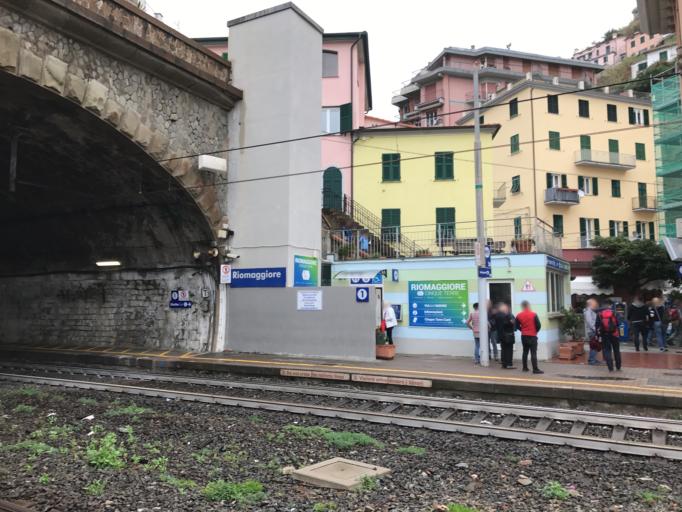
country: IT
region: Liguria
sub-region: Provincia di La Spezia
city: Riomaggiore
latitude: 44.1007
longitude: 9.7360
